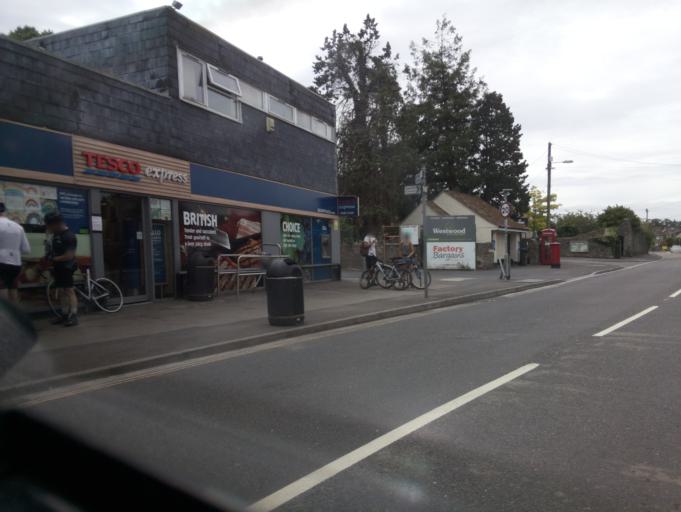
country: GB
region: England
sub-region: Somerset
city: Cheddar
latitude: 51.2757
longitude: -2.7783
